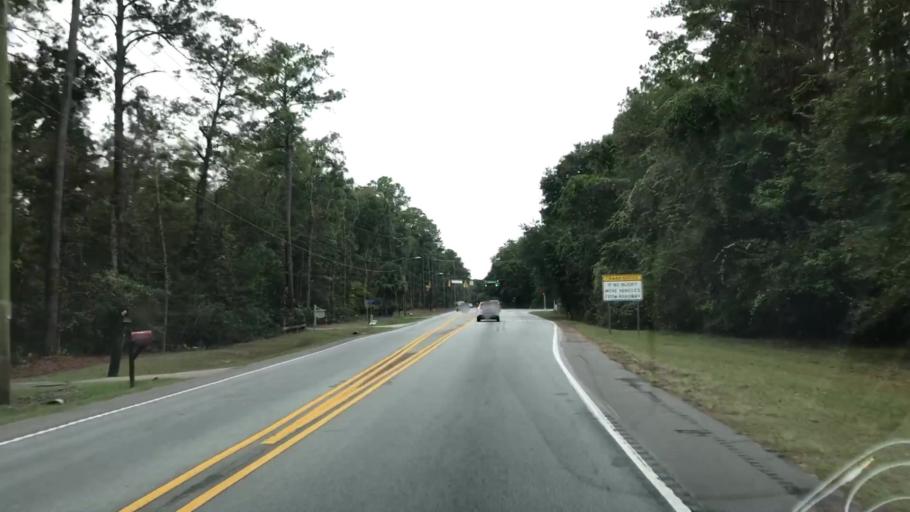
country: US
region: South Carolina
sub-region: Beaufort County
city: Bluffton
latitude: 32.2353
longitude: -80.9010
